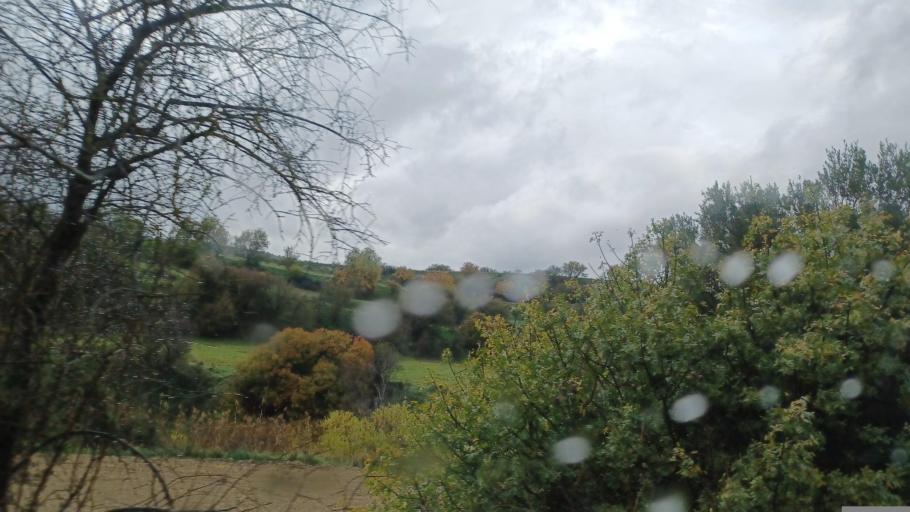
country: CY
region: Pafos
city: Mesogi
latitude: 34.8604
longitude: 32.5414
